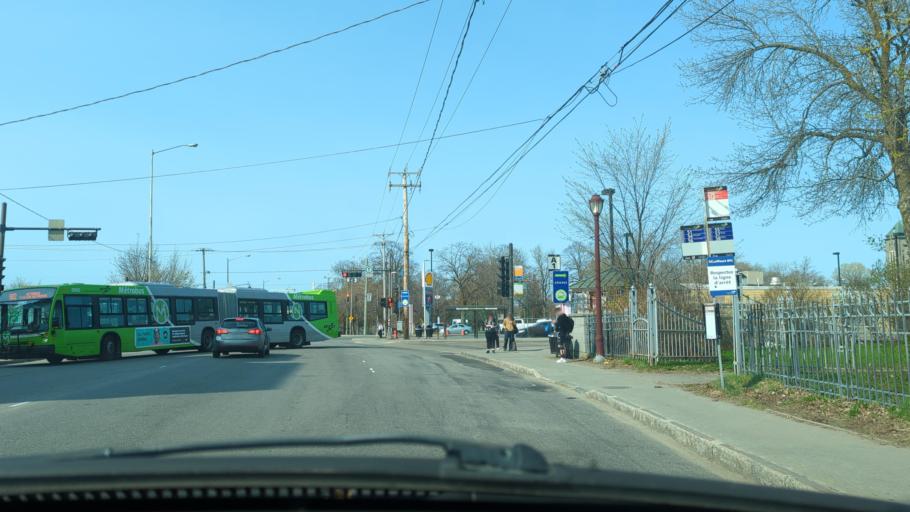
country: CA
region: Quebec
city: Quebec
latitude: 46.8470
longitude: -71.2155
